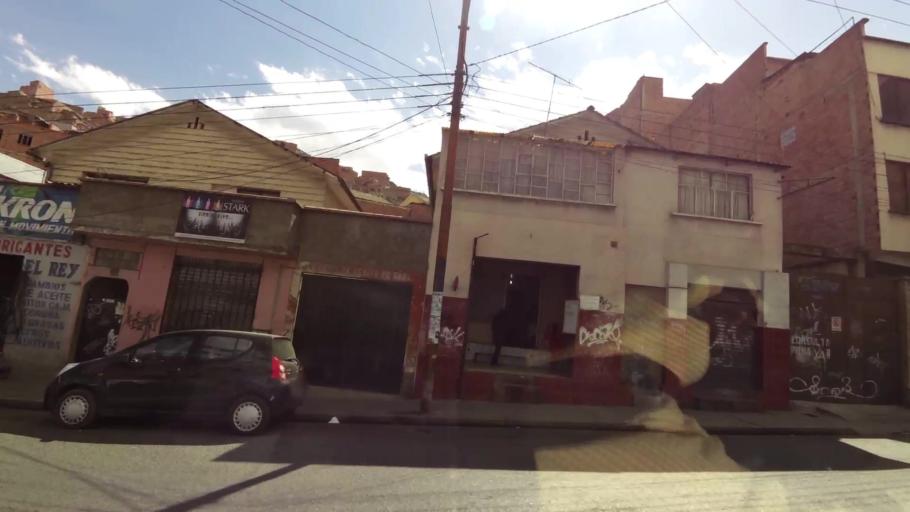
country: BO
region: La Paz
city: La Paz
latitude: -16.4855
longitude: -68.1239
